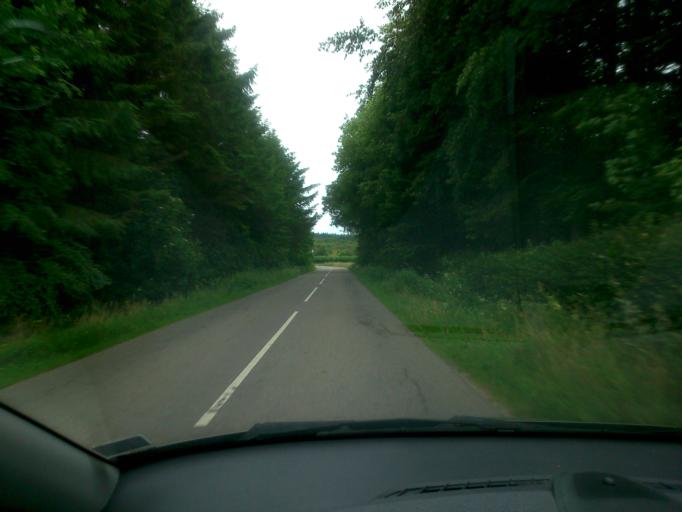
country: DK
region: Central Jutland
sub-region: Ringkobing-Skjern Kommune
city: Skjern
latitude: 56.0076
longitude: 8.4831
